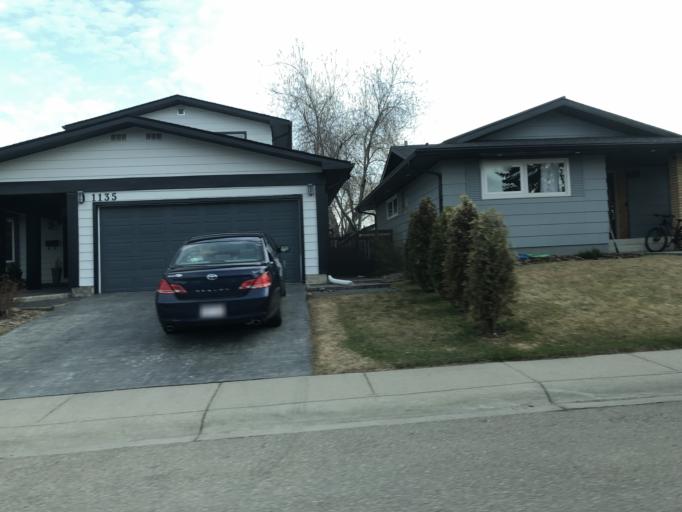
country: CA
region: Alberta
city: Calgary
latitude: 50.9390
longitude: -114.0381
